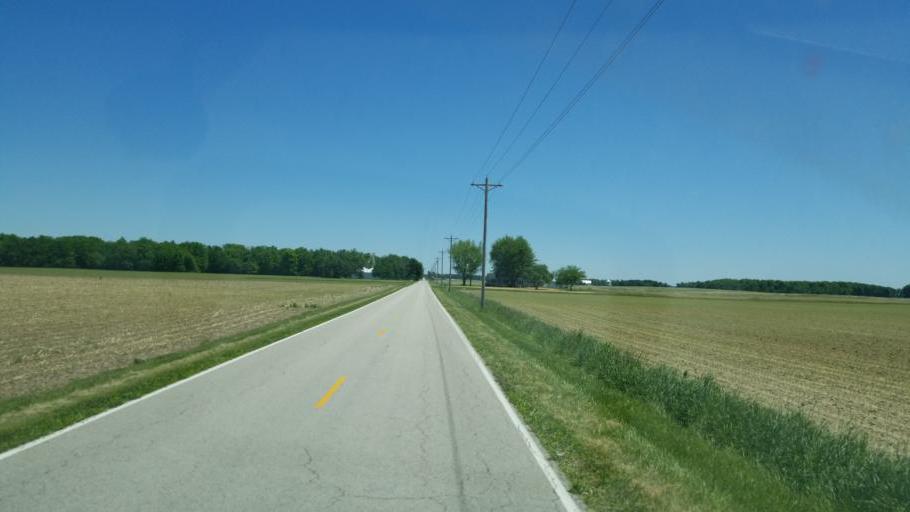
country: US
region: Ohio
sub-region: Darke County
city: Ansonia
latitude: 40.2649
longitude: -84.6925
